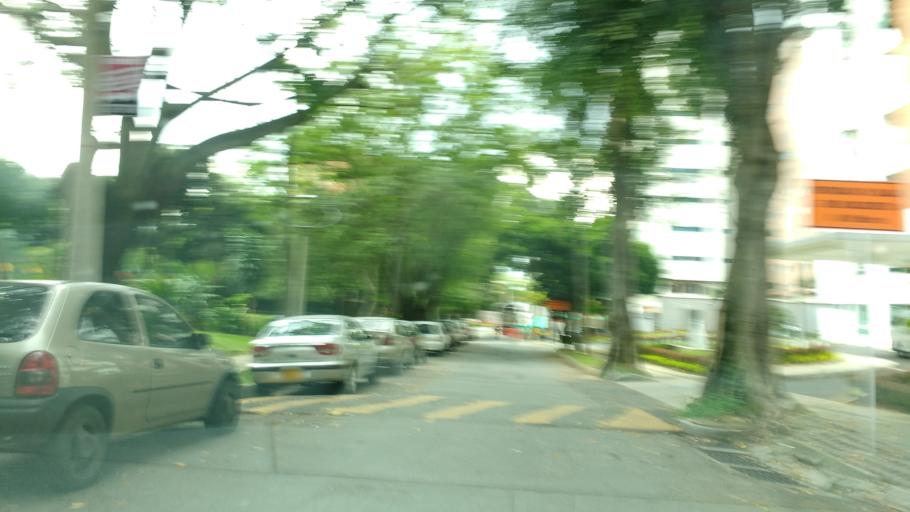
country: CO
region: Antioquia
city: Envigado
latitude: 6.1878
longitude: -75.5801
